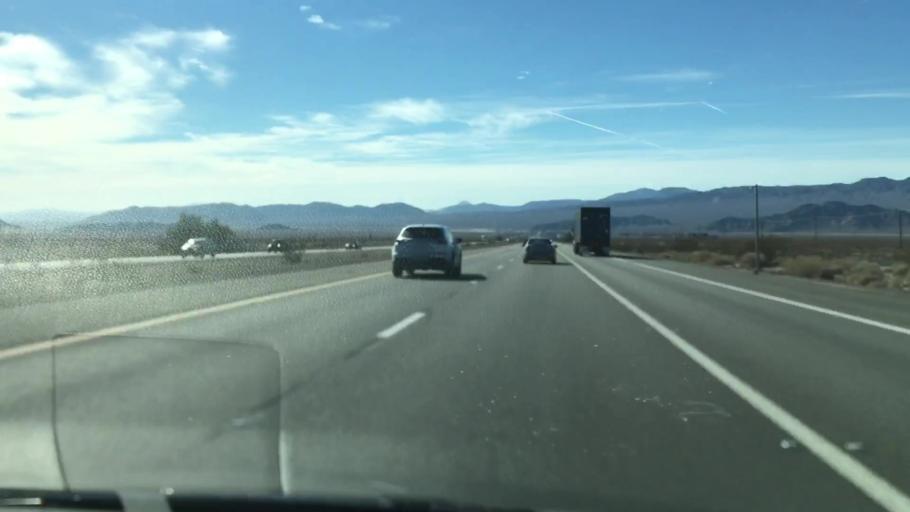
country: US
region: Nevada
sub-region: Clark County
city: Sandy Valley
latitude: 35.3045
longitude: -116.0138
